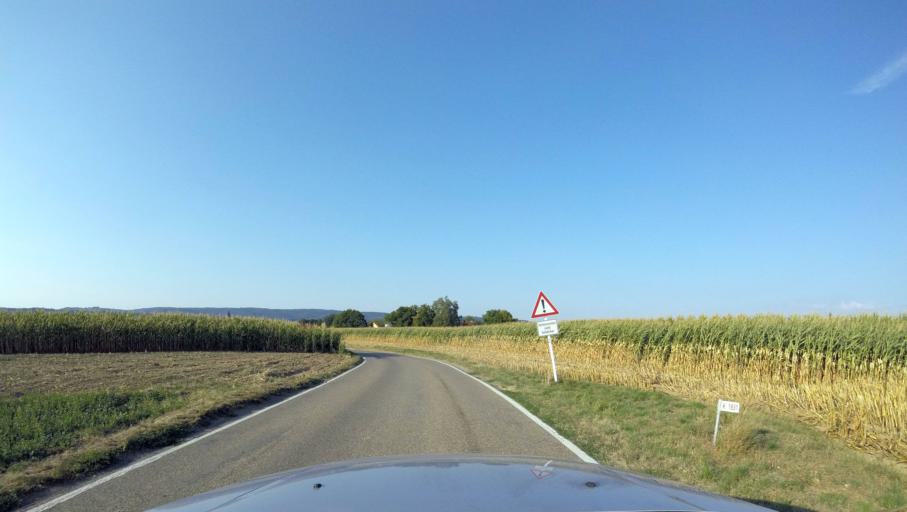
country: DE
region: Baden-Wuerttemberg
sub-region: Regierungsbezirk Stuttgart
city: Aspach
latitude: 48.9556
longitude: 9.4013
